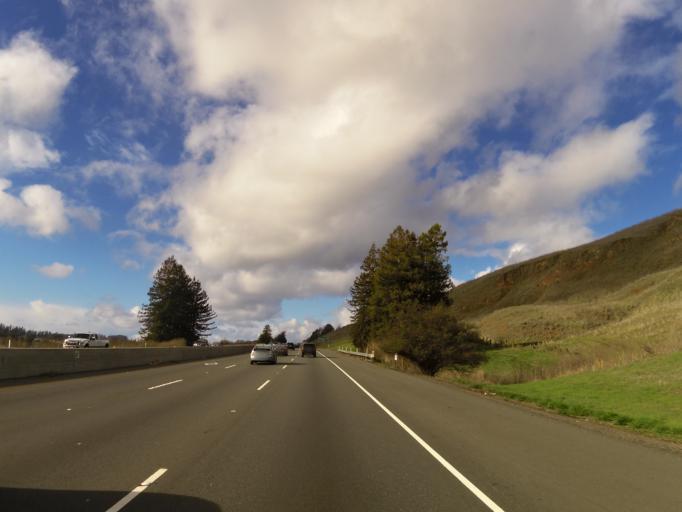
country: US
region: California
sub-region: Sonoma County
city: Penngrove
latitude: 38.2888
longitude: -122.6916
